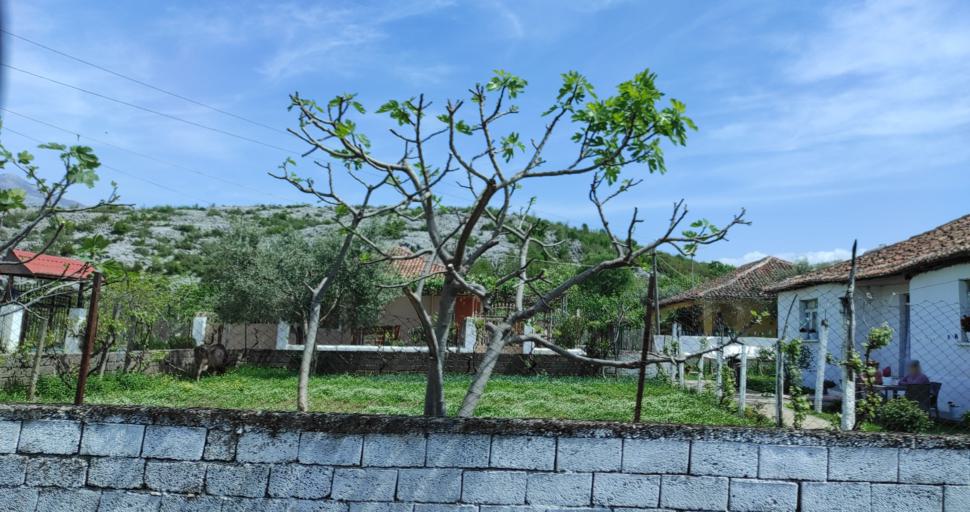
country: AL
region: Shkoder
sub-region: Rrethi i Malesia e Madhe
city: Gruemire
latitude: 42.1234
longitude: 19.5579
